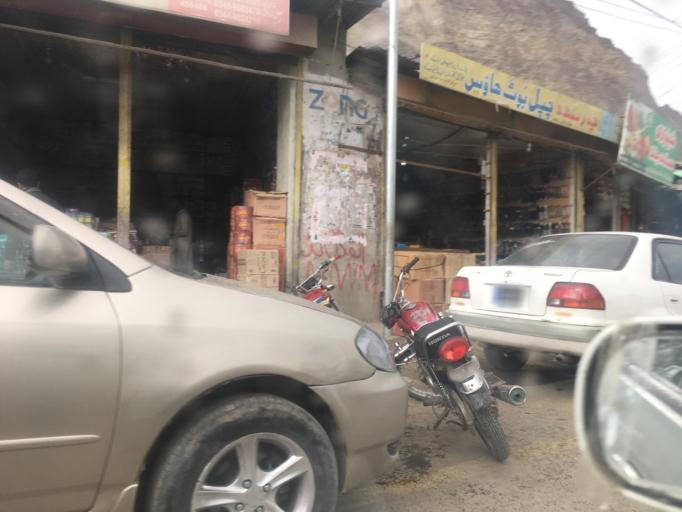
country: PK
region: Gilgit-Baltistan
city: Skardu
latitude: 35.3011
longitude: 75.6300
